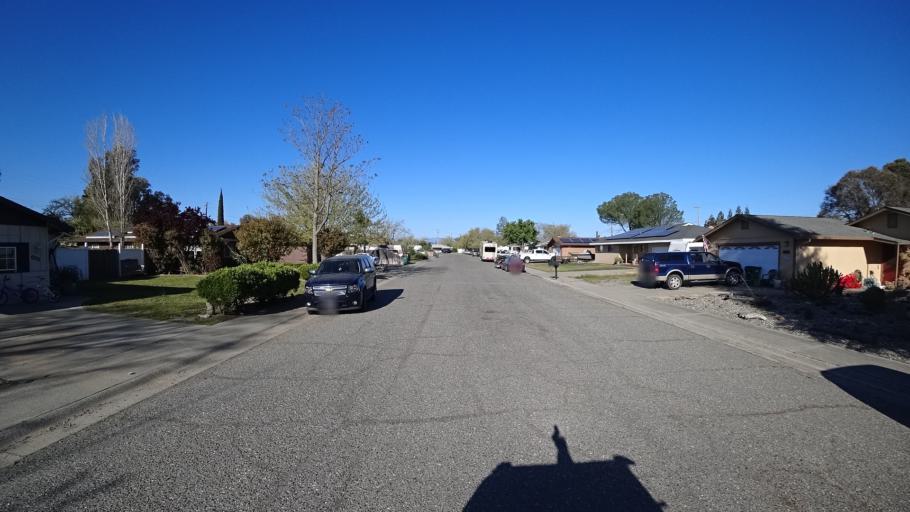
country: US
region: California
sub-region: Glenn County
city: Orland
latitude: 39.7591
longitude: -122.2228
